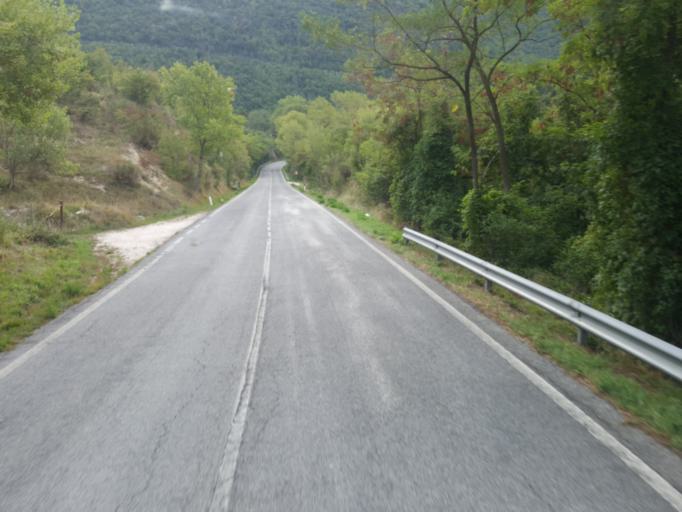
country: IT
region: The Marches
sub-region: Provincia di Ancona
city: Fabriano
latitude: 43.3236
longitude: 12.8345
